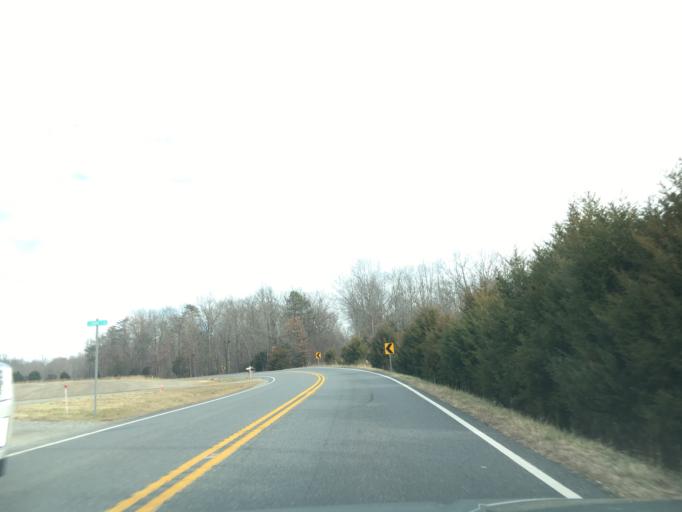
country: US
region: Virginia
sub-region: Goochland County
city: Goochland
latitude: 37.7995
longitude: -77.8665
